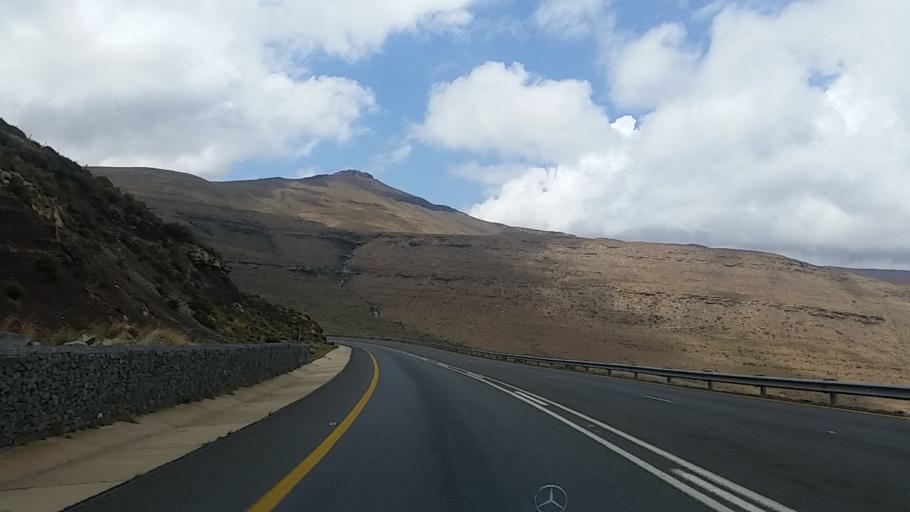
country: ZA
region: Eastern Cape
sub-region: Chris Hani District Municipality
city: Middelburg
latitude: -31.8447
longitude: 24.8722
